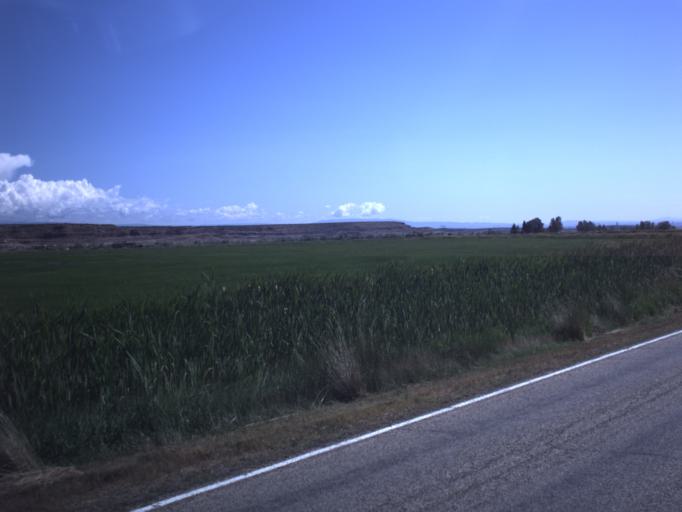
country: US
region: Utah
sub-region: Duchesne County
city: Roosevelt
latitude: 40.2580
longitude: -110.1754
